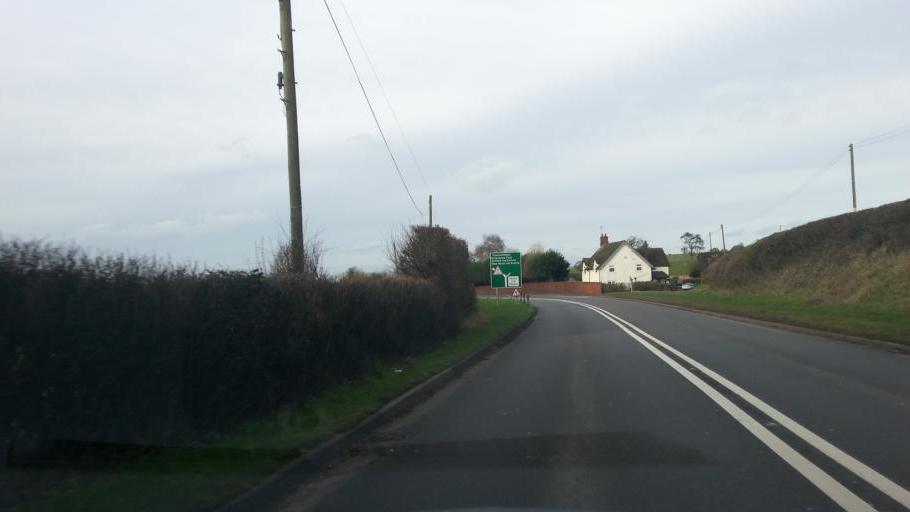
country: GB
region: England
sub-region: Staffordshire
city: Colwich
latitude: 52.8142
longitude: -2.0007
